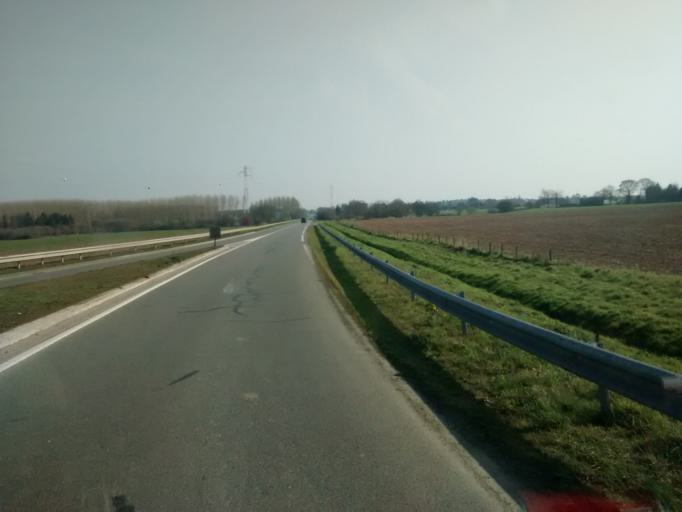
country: FR
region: Brittany
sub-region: Departement d'Ille-et-Vilaine
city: Chavagne
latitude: 48.0773
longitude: -1.7932
